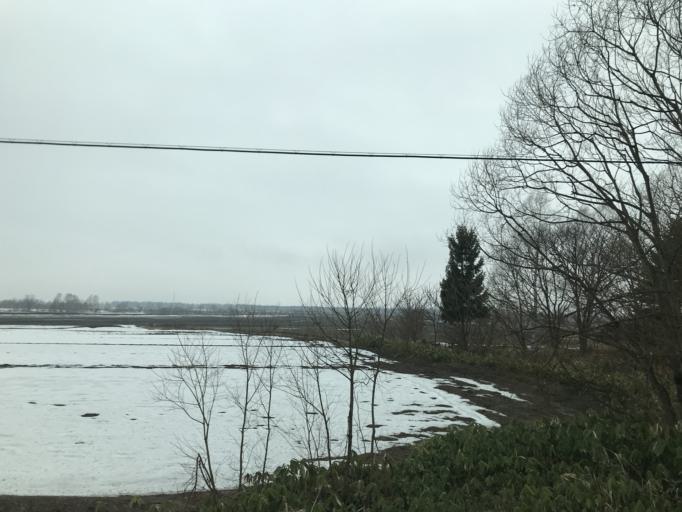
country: JP
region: Hokkaido
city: Nayoro
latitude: 44.1064
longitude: 142.3902
